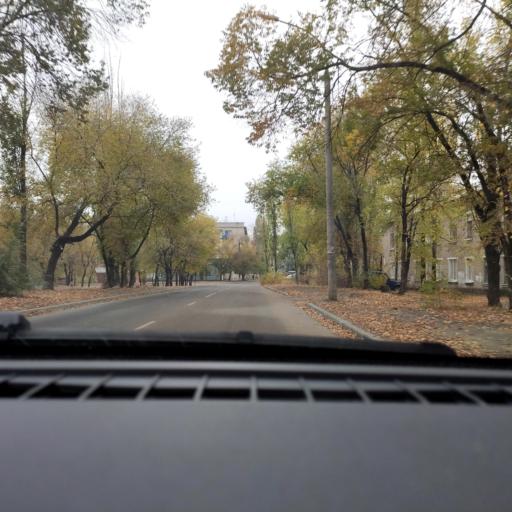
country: RU
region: Voronezj
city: Maslovka
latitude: 51.6148
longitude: 39.2438
